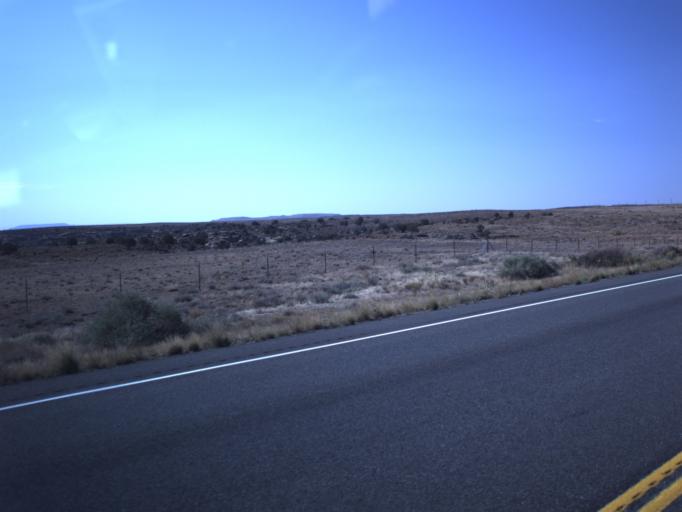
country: US
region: Utah
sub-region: San Juan County
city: Blanding
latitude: 37.4127
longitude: -109.4844
